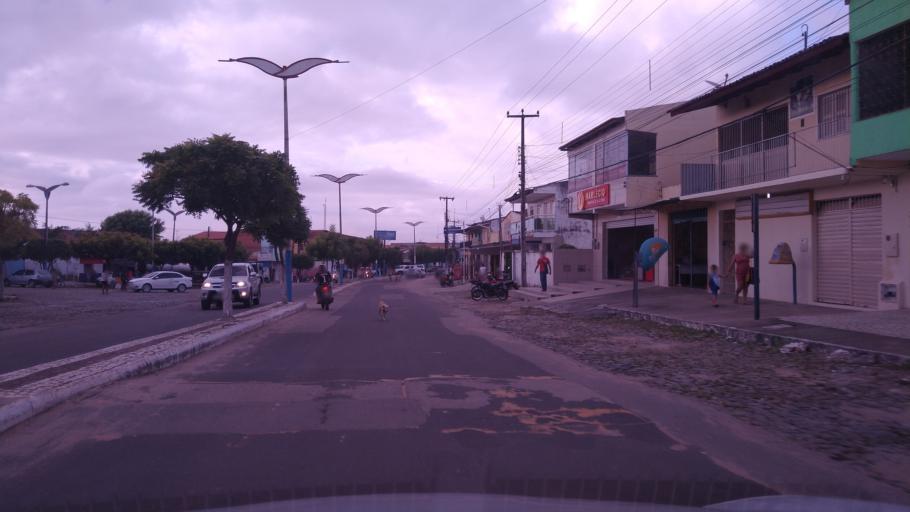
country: BR
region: Ceara
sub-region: Chorozinho
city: Chorozinho
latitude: -4.3008
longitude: -38.4980
